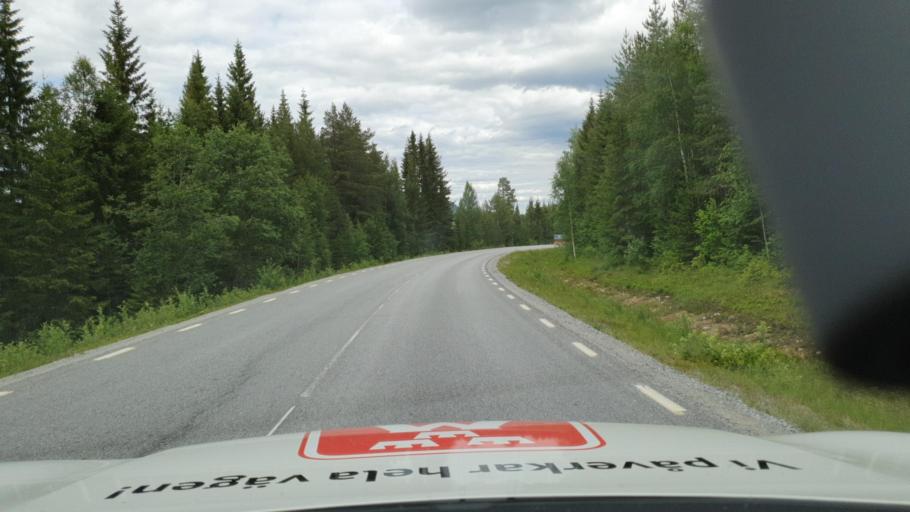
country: SE
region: Vaesterbotten
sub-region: Bjurholms Kommun
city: Bjurholm
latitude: 63.9000
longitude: 19.0749
